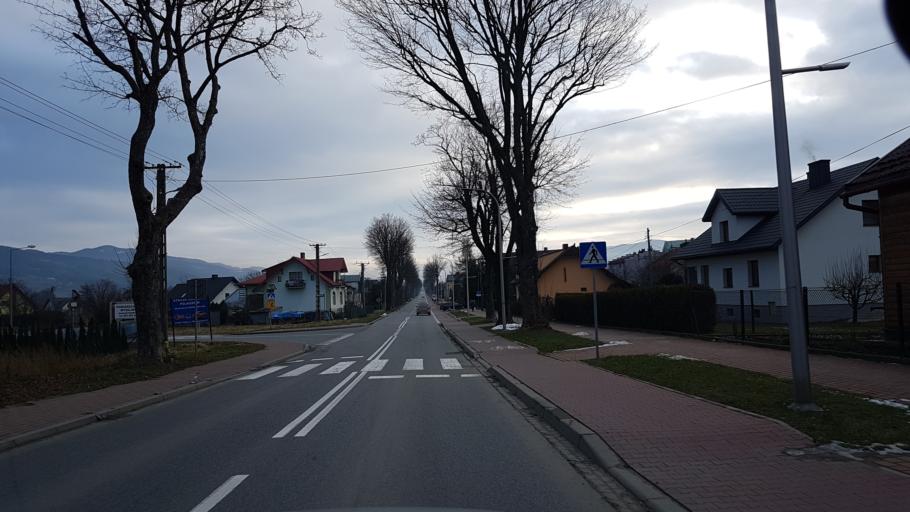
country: PL
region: Lesser Poland Voivodeship
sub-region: Powiat nowosadecki
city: Stary Sacz
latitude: 49.5558
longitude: 20.6384
